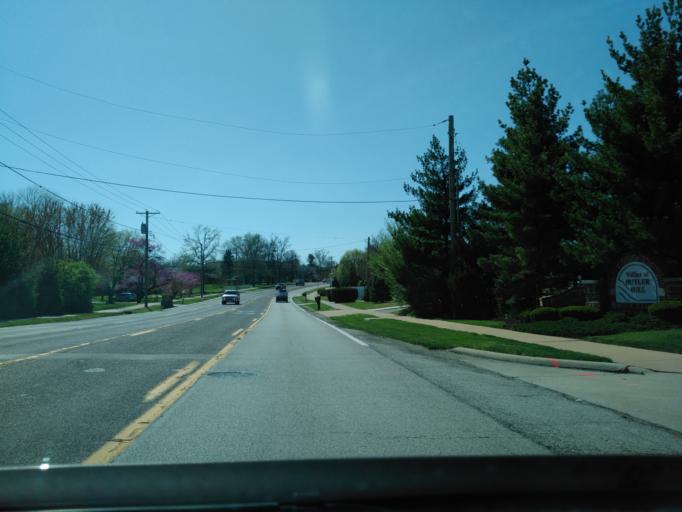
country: US
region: Missouri
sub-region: Saint Louis County
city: Concord
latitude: 38.4858
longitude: -90.3612
